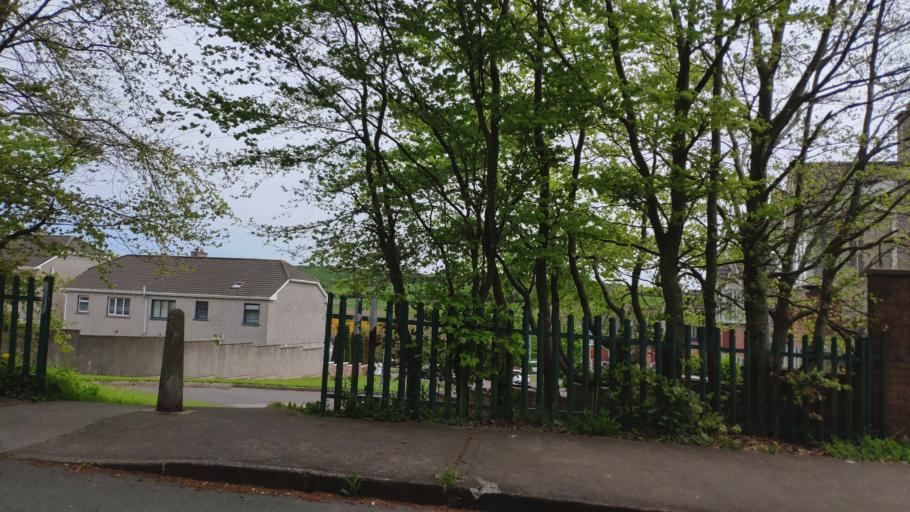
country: IE
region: Munster
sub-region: County Cork
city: Cork
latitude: 51.9236
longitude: -8.4588
